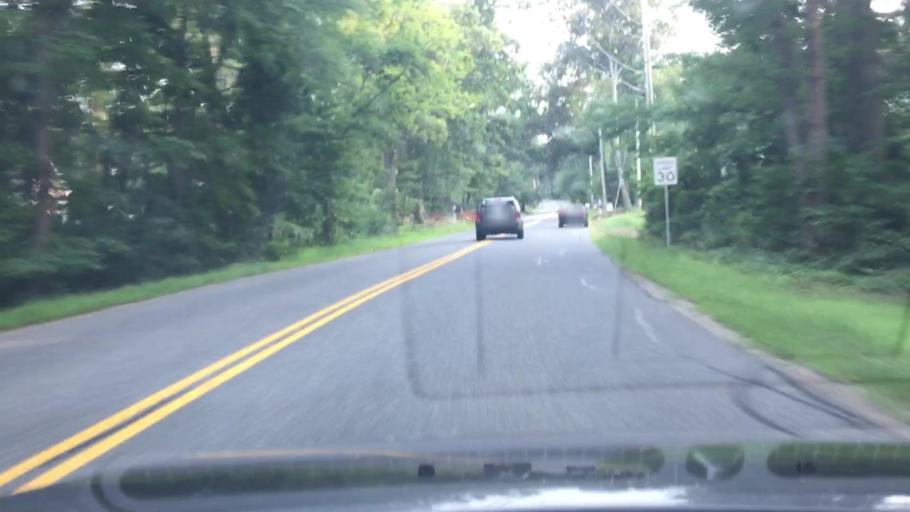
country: US
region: Massachusetts
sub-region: Middlesex County
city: Hopkinton
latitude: 42.1894
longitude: -71.5393
